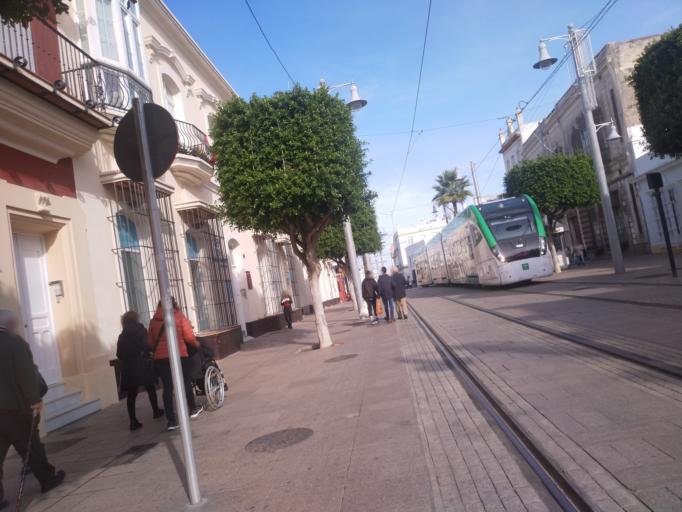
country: ES
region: Andalusia
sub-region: Provincia de Cadiz
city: San Fernando
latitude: 36.4614
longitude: -6.2004
